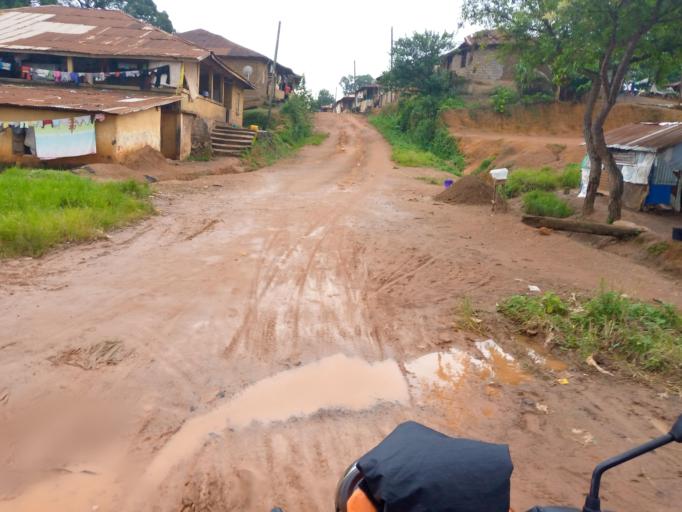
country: SL
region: Eastern Province
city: Kenema
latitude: 7.8687
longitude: -11.1884
